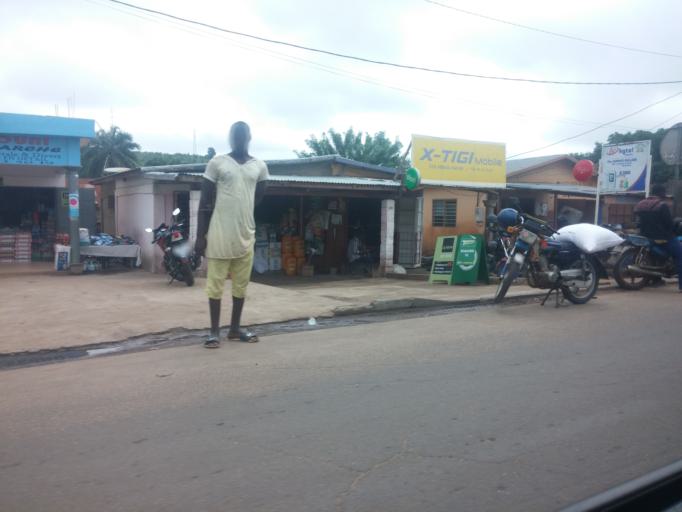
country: TG
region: Plateaux
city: Atakpame
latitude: 7.5169
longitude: 1.1477
